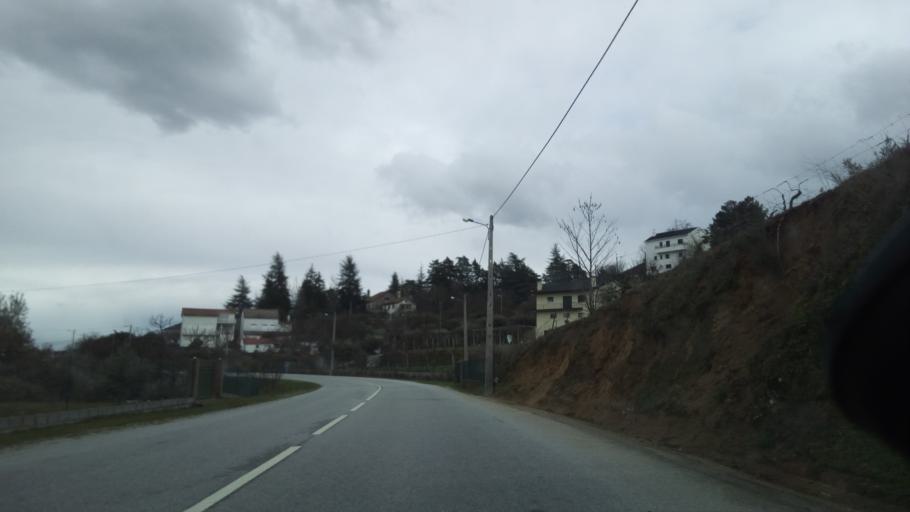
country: PT
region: Guarda
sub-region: Manteigas
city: Manteigas
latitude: 40.4996
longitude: -7.5921
